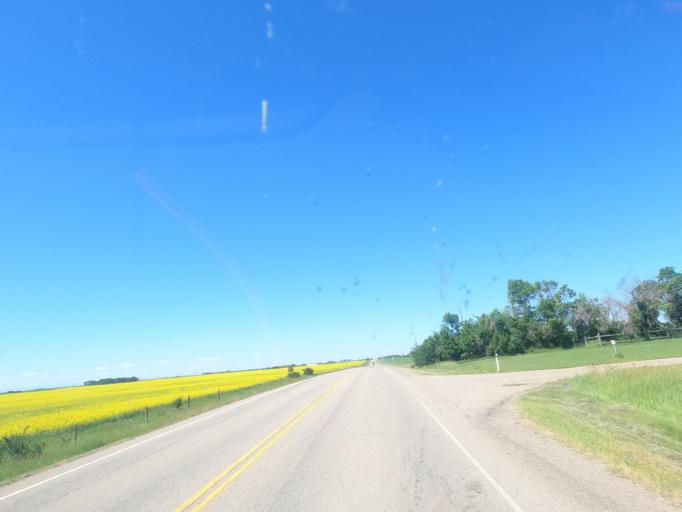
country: CA
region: Alberta
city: Chestermere
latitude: 51.1547
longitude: -113.7785
